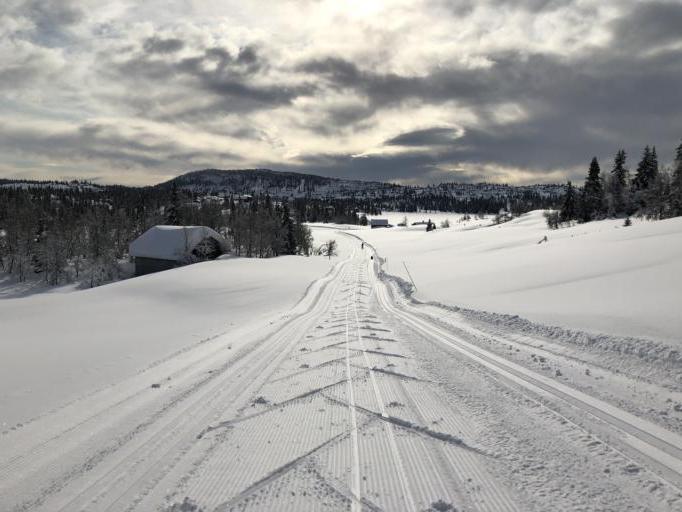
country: NO
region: Oppland
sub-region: Gausdal
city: Segalstad bru
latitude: 61.3186
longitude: 10.0585
